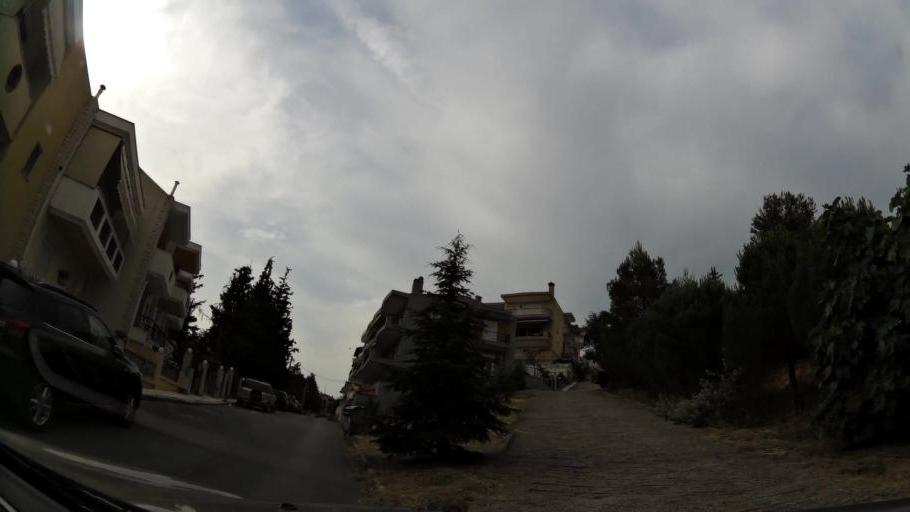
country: GR
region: Central Macedonia
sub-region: Nomos Thessalonikis
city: Oraiokastro
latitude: 40.7309
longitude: 22.9248
